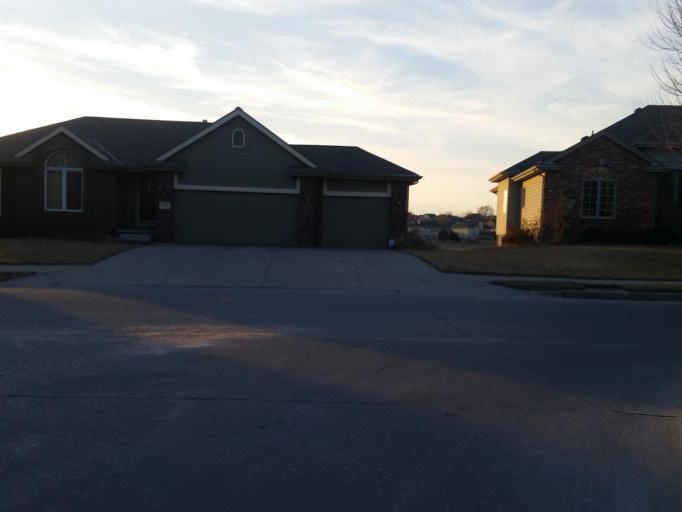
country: US
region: Nebraska
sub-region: Sarpy County
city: Papillion
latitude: 41.1525
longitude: -95.9993
